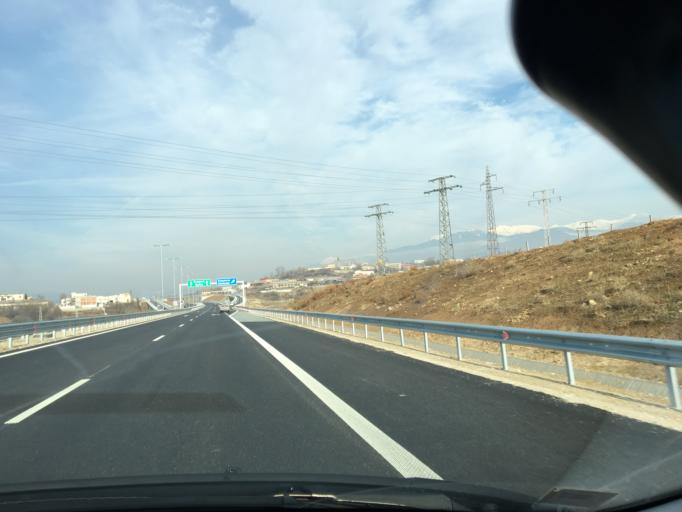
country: BG
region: Blagoevgrad
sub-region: Obshtina Sandanski
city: Sandanski
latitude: 41.5352
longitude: 23.2582
